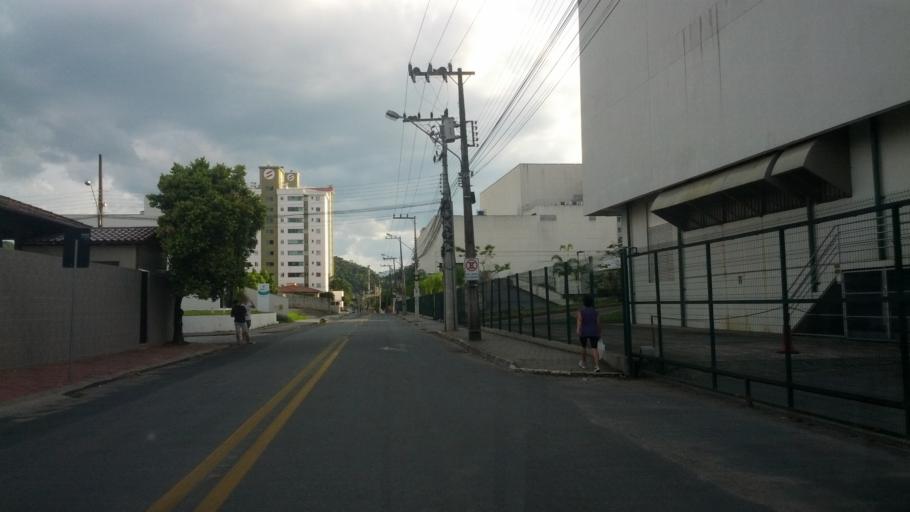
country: BR
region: Santa Catarina
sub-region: Blumenau
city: Blumenau
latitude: -26.8860
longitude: -49.0675
